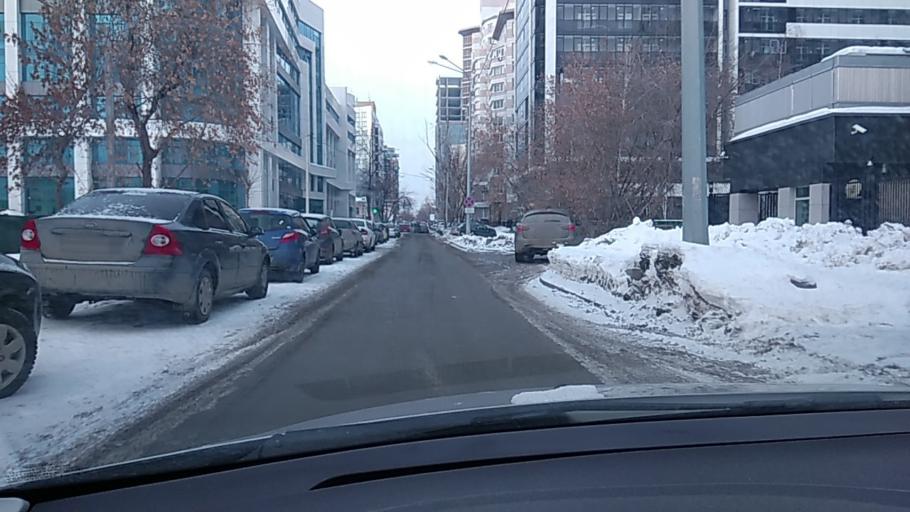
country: RU
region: Sverdlovsk
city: Yekaterinburg
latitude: 56.8285
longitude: 60.6118
